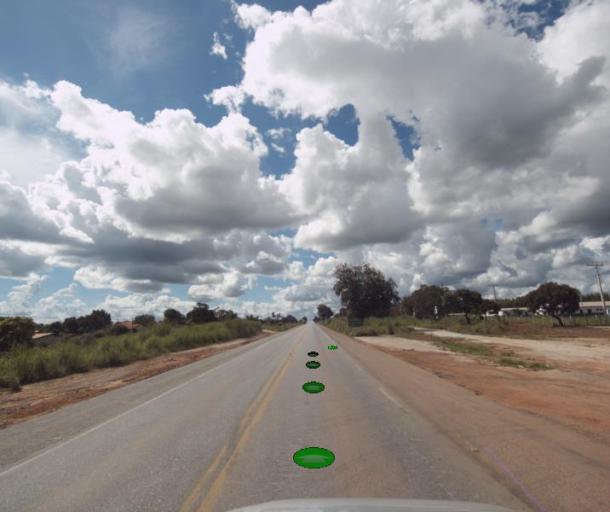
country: BR
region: Goias
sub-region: Porangatu
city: Porangatu
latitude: -13.4255
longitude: -49.1303
